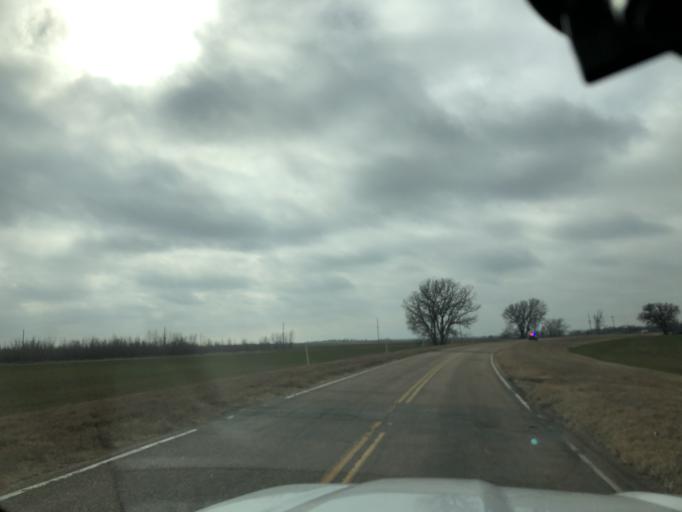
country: US
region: Kansas
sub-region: Stafford County
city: Stafford
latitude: 37.9579
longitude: -98.4004
